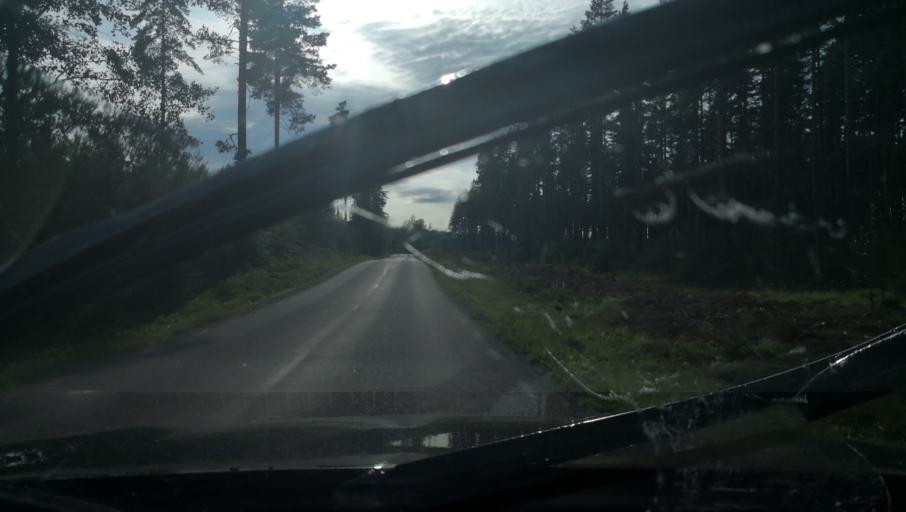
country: SE
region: Dalarna
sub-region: Smedjebackens Kommun
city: Smedjebacken
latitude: 60.0409
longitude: 15.3029
